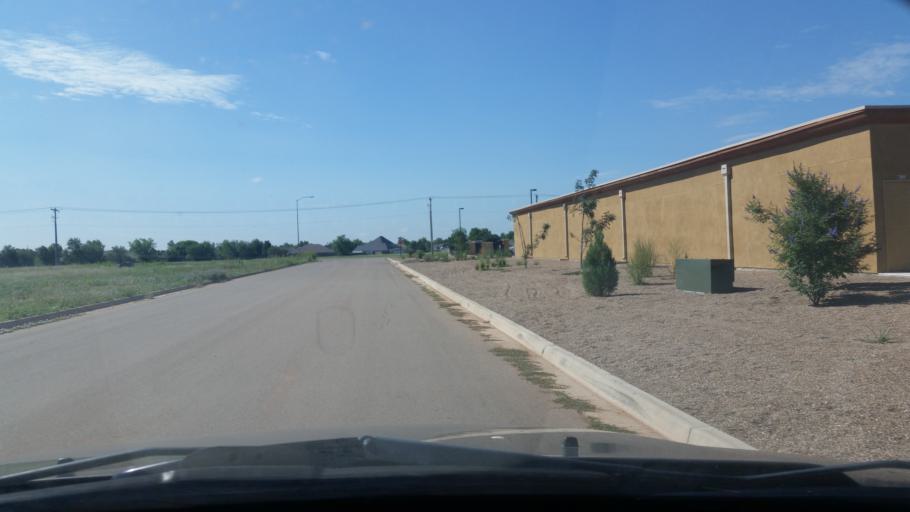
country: US
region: New Mexico
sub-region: Curry County
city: Clovis
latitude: 34.4351
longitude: -103.1738
